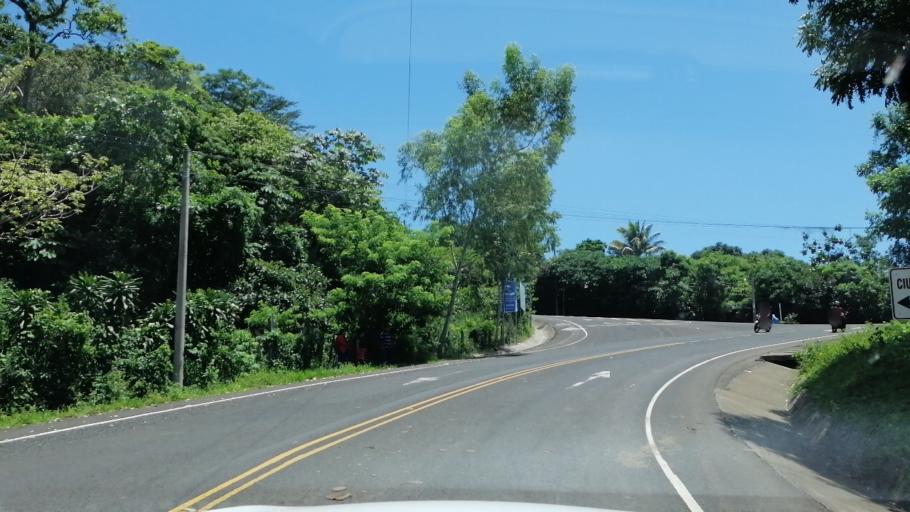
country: SV
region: San Miguel
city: Ciudad Barrios
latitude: 13.7950
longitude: -88.2865
